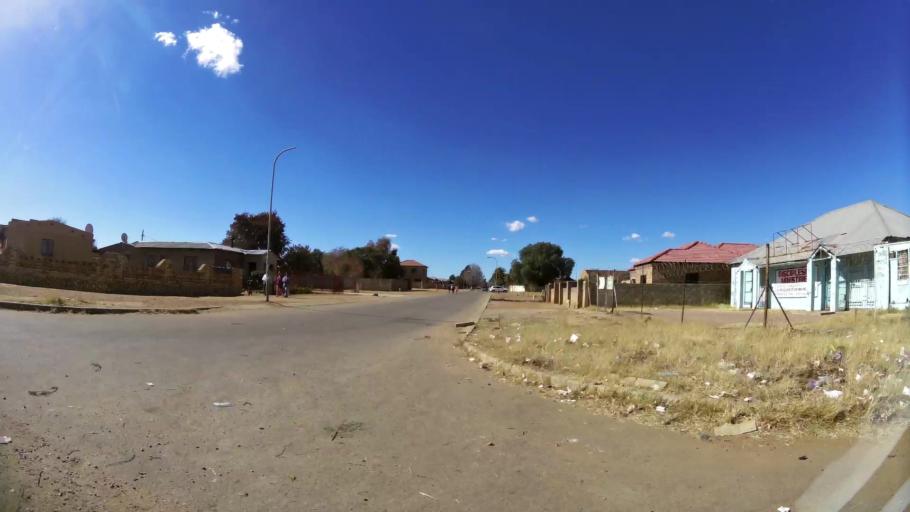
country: ZA
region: North-West
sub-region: Dr Kenneth Kaunda District Municipality
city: Klerksdorp
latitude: -26.8734
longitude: 26.5804
